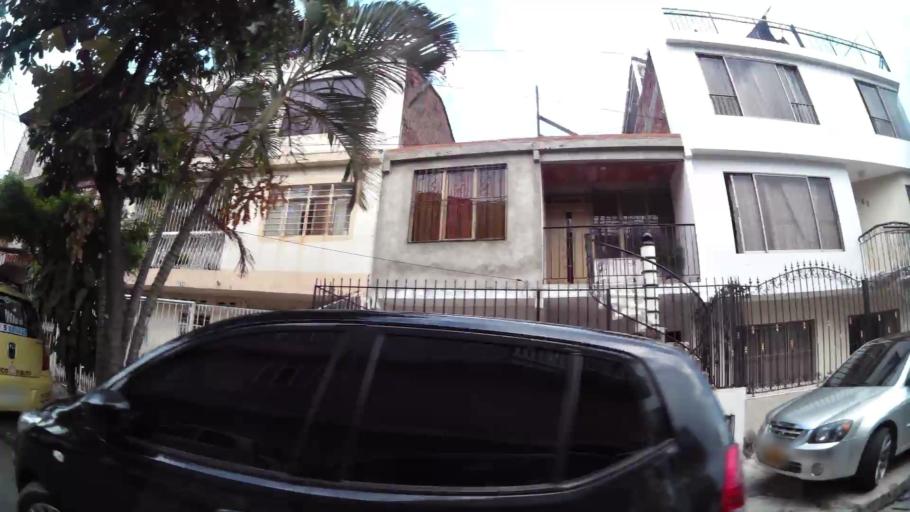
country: CO
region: Valle del Cauca
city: Cali
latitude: 3.4376
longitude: -76.5233
